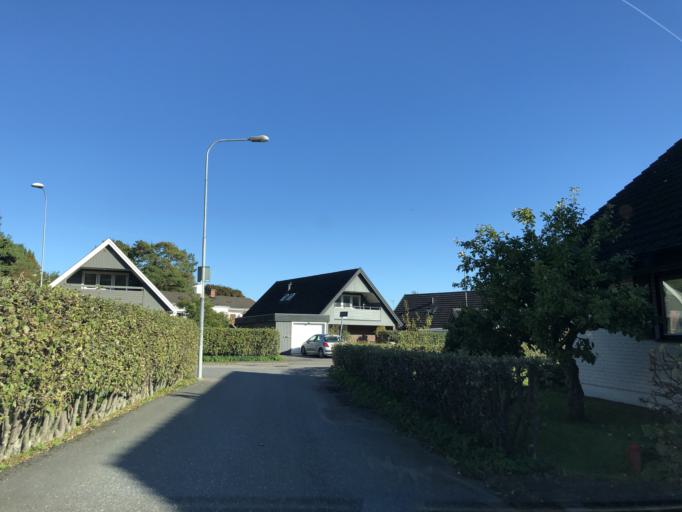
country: SE
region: Vaestra Goetaland
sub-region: Goteborg
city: Majorna
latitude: 57.6552
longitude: 11.8604
